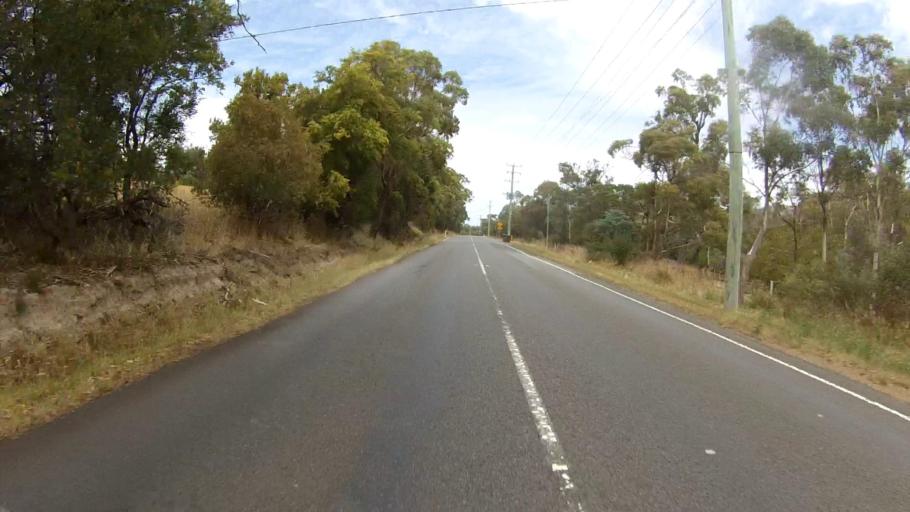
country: AU
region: Tasmania
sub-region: Clarence
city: Acton Park
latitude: -42.8703
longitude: 147.4836
